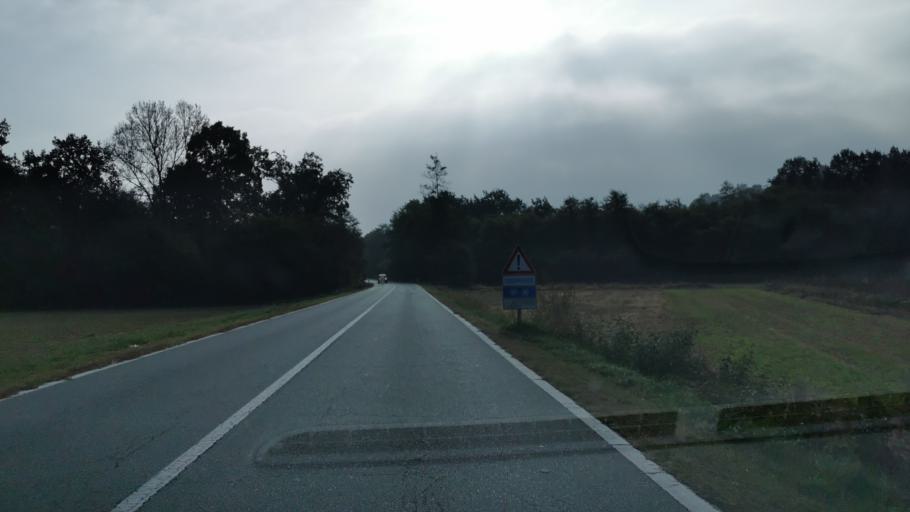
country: IT
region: Piedmont
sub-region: Provincia di Torino
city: Front
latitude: 45.2684
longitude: 7.6837
